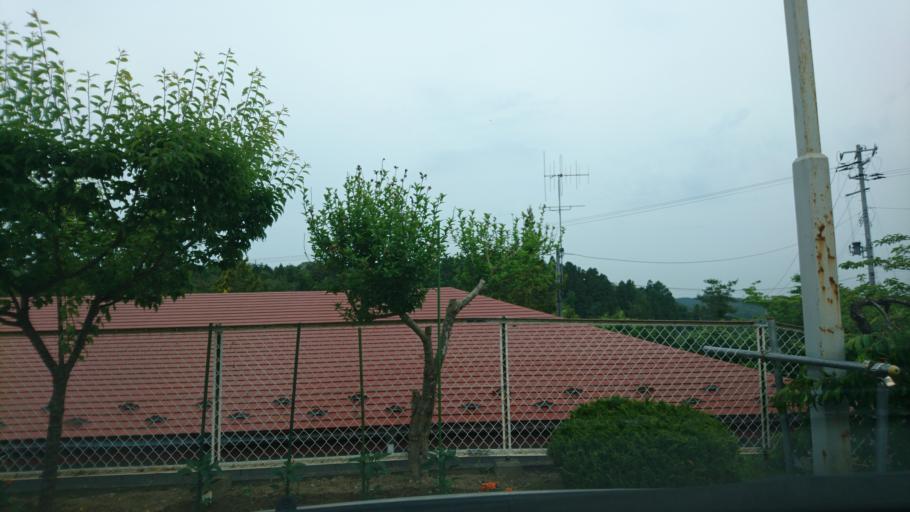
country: JP
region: Iwate
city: Ichinoseki
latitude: 38.8817
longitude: 141.1385
